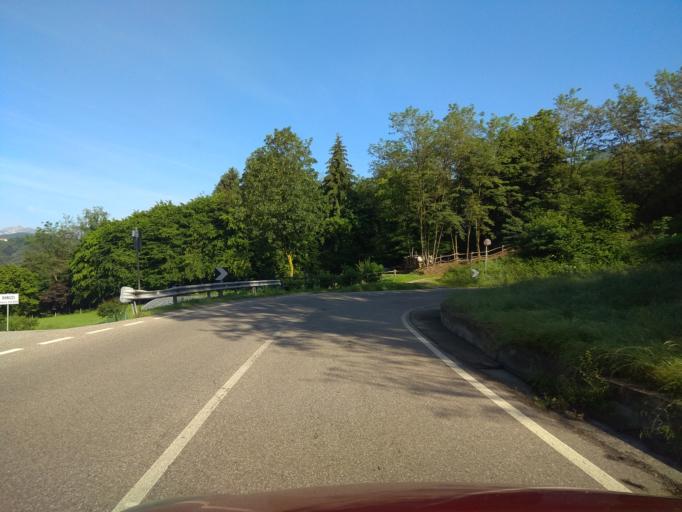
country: IT
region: Piedmont
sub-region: Provincia di Biella
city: Valle Mosso
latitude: 45.6387
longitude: 8.1456
